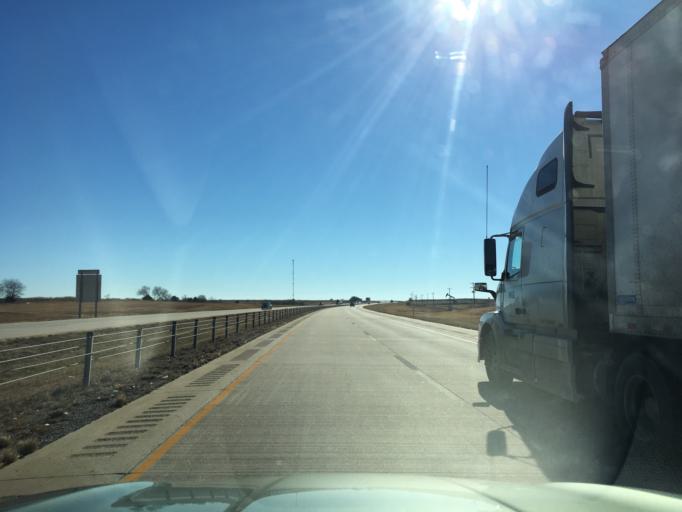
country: US
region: Oklahoma
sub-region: Kay County
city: Tonkawa
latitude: 36.5211
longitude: -97.3383
